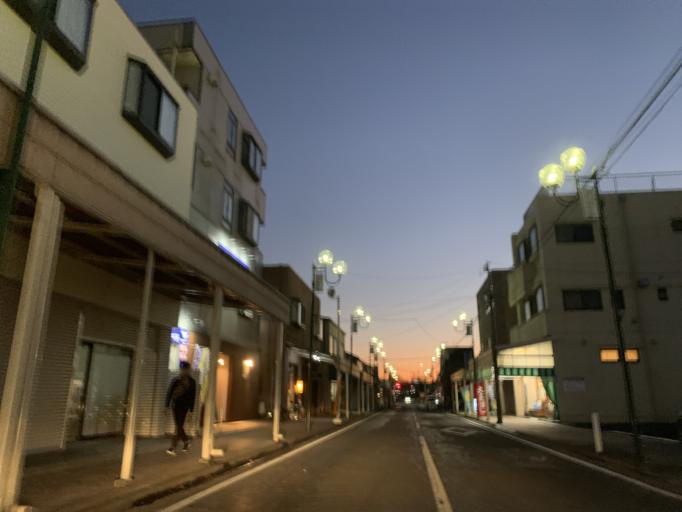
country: JP
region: Chiba
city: Nagareyama
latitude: 35.8967
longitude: 139.9097
